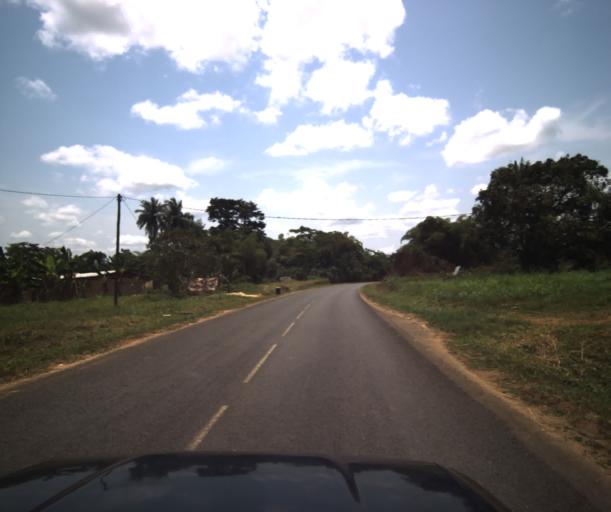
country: CM
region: Centre
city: Eseka
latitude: 3.6969
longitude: 10.7867
